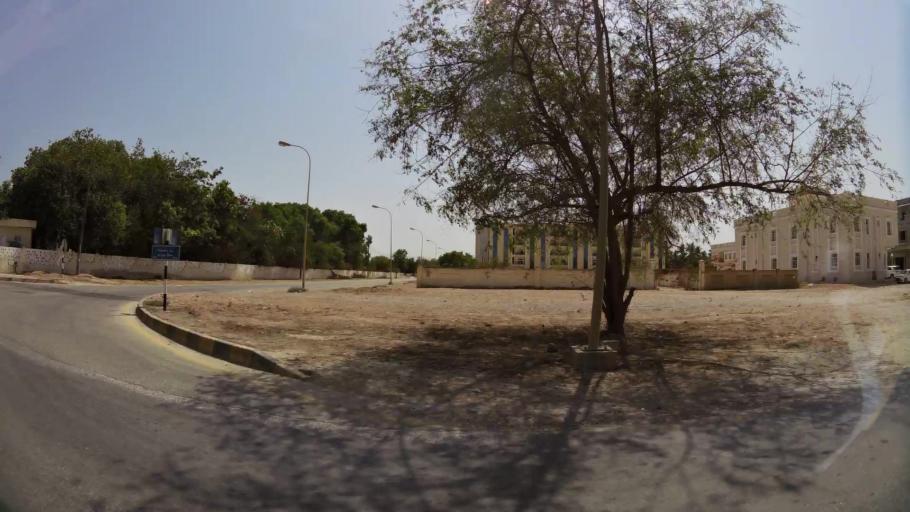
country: OM
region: Zufar
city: Salalah
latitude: 17.0149
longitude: 54.0730
